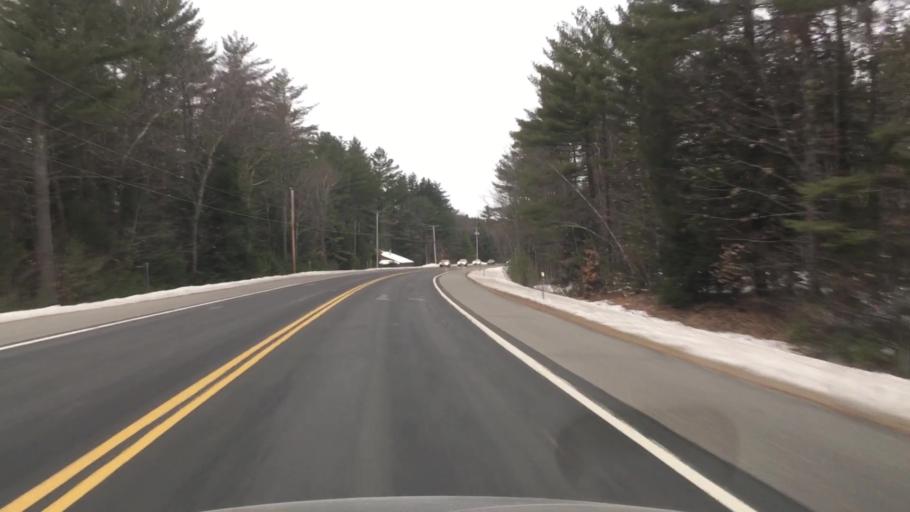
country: US
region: New Hampshire
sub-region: Merrimack County
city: Henniker
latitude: 43.2108
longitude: -71.8639
